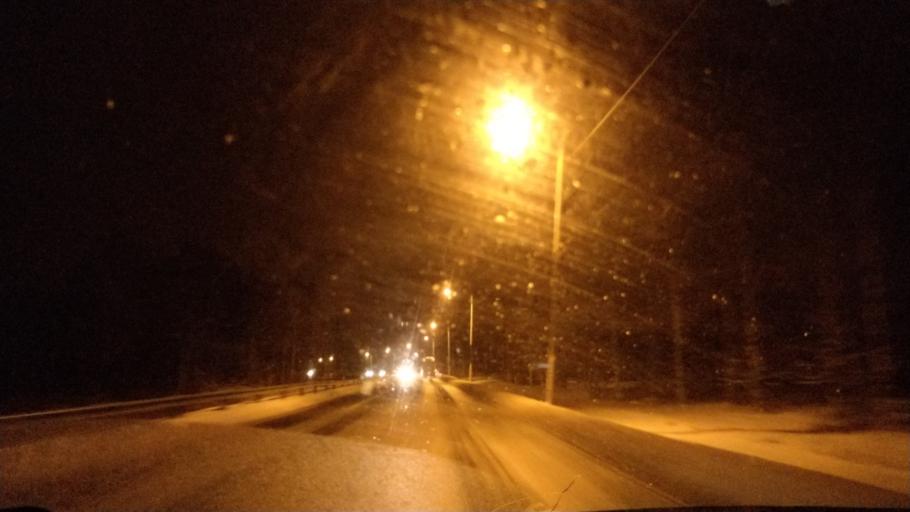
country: FI
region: Lapland
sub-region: Rovaniemi
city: Rovaniemi
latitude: 66.2873
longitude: 25.3448
